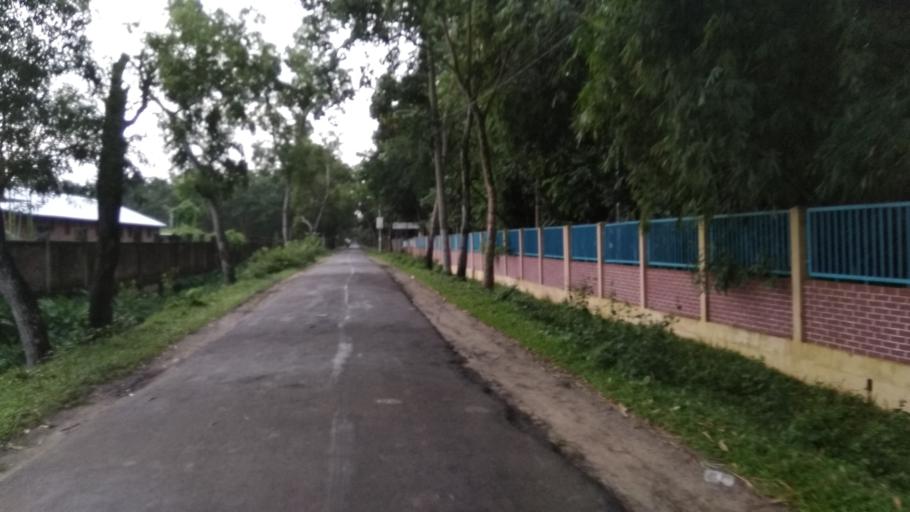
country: IN
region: Tripura
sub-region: Dhalai
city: Kamalpur
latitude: 24.2990
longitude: 91.7368
